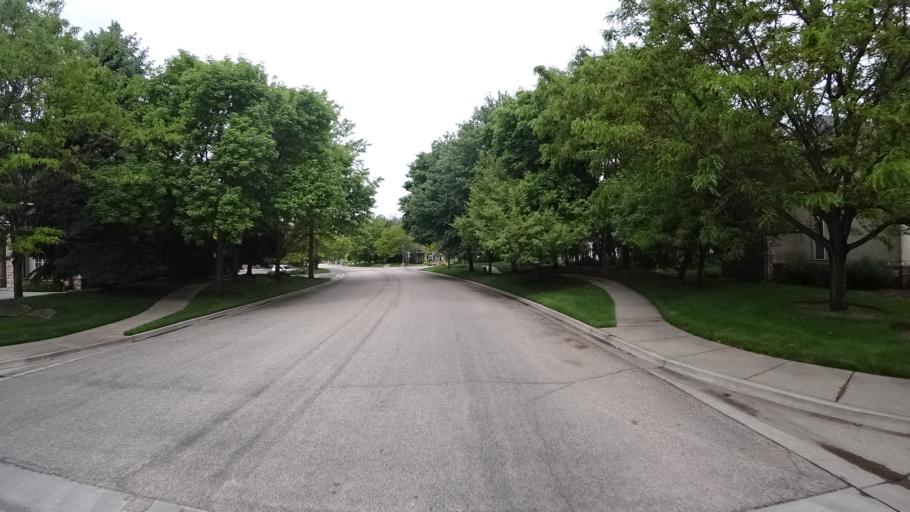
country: US
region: Idaho
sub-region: Ada County
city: Eagle
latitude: 43.6829
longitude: -116.3509
